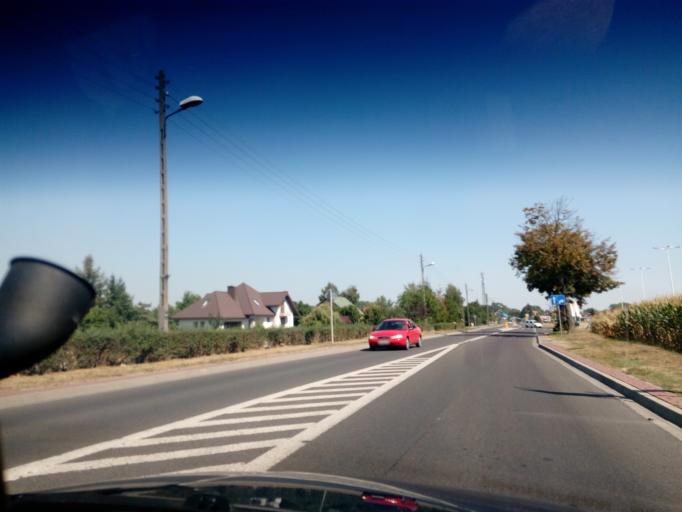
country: PL
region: Lublin Voivodeship
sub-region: Powiat hrubieszowski
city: Hrubieszow
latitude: 50.7961
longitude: 23.8968
